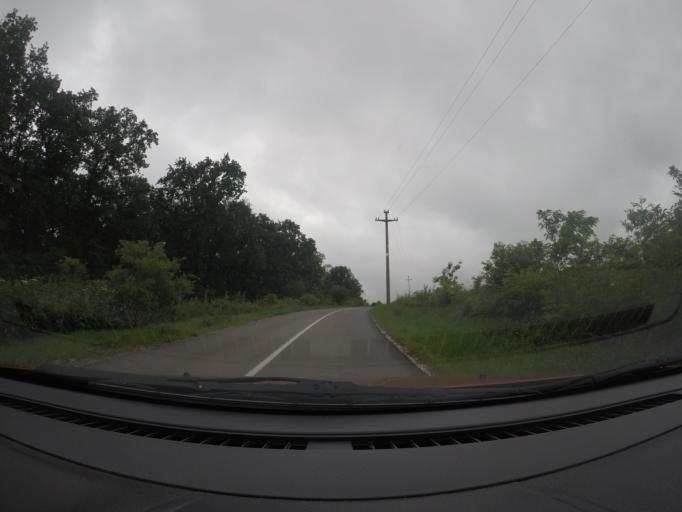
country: RS
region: Central Serbia
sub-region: Belgrade
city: Sopot
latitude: 44.5639
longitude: 20.5546
